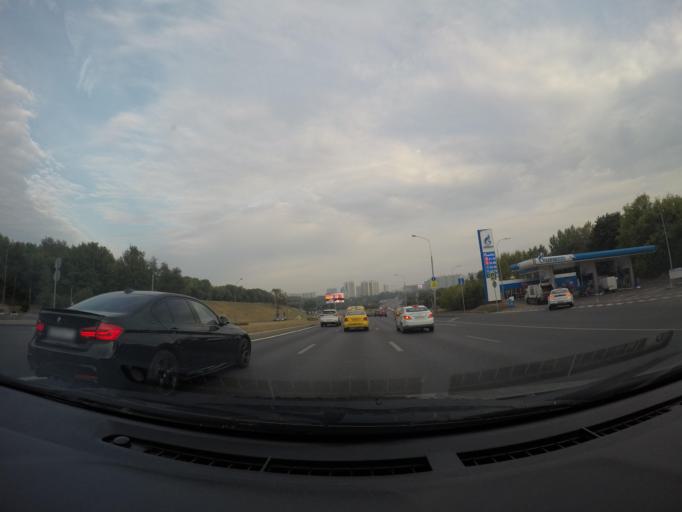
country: RU
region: Moskovskaya
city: Kur'yanovo
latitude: 55.6334
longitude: 37.7016
